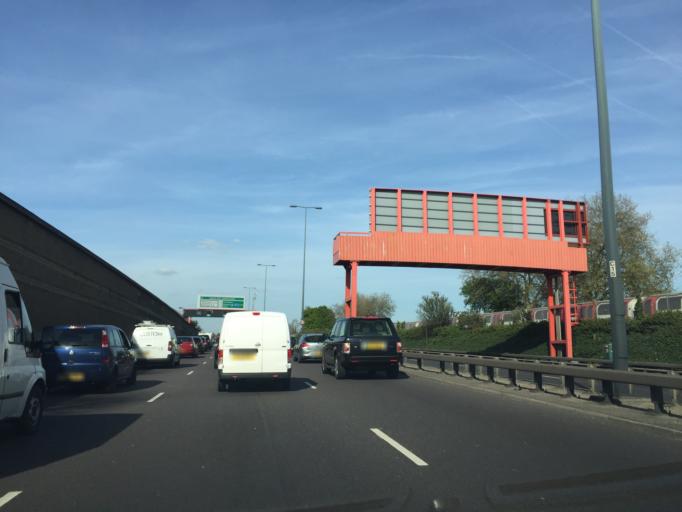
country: GB
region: England
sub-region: Greater London
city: Walthamstow
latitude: 51.5582
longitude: -0.0037
